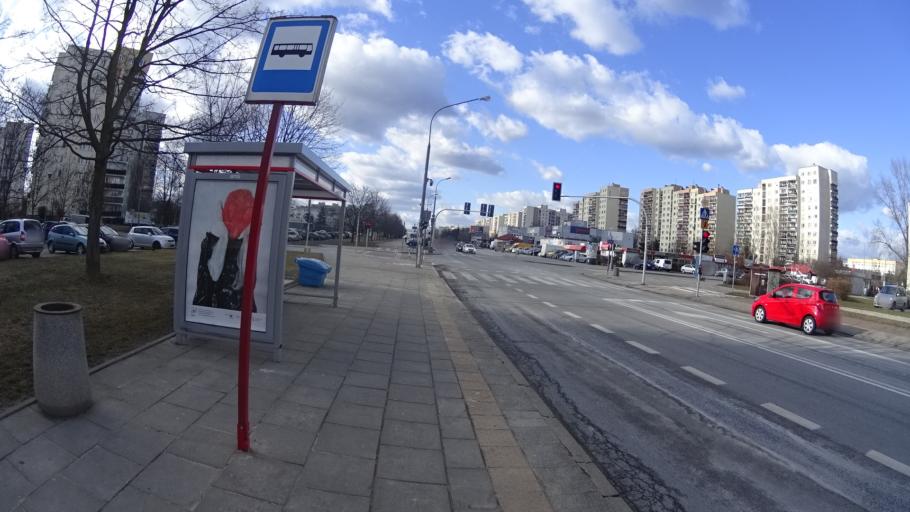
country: PL
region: Masovian Voivodeship
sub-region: Warszawa
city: Bialoleka
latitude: 52.3126
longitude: 20.9582
